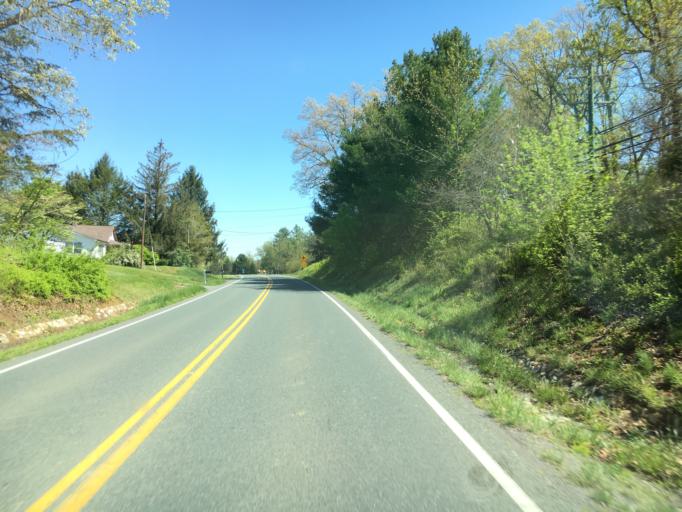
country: US
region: Virginia
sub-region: Augusta County
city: Crimora
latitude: 38.1461
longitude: -78.8412
